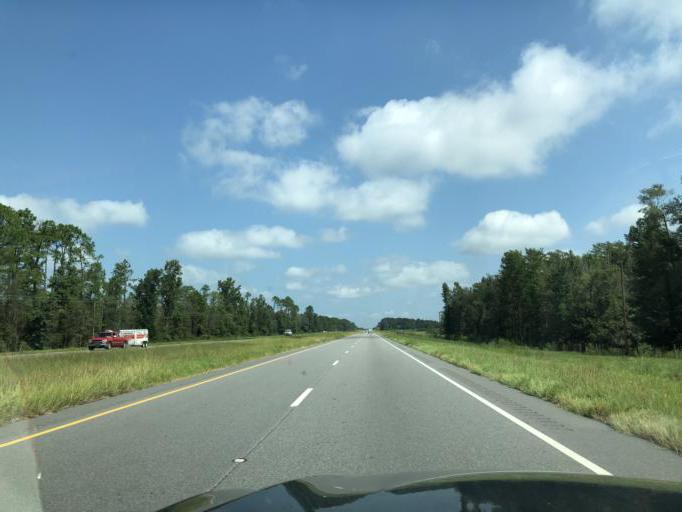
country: US
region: Alabama
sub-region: Houston County
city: Cottonwood
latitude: 31.0283
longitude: -85.4068
